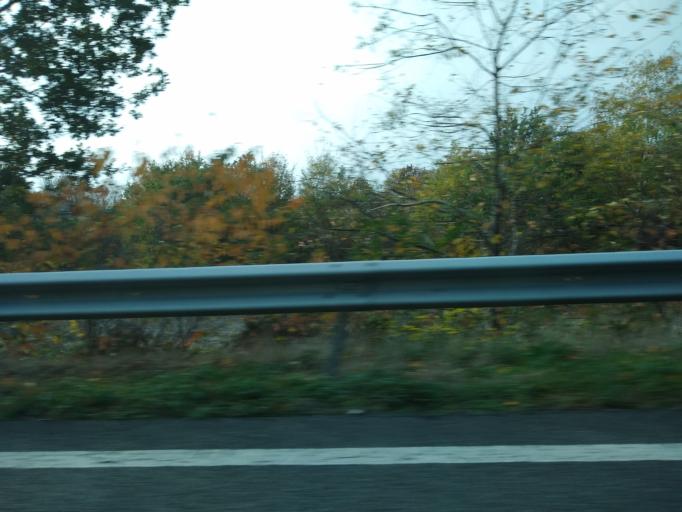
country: DE
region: Lower Saxony
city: Oldenburg
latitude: 53.1157
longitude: 8.2746
